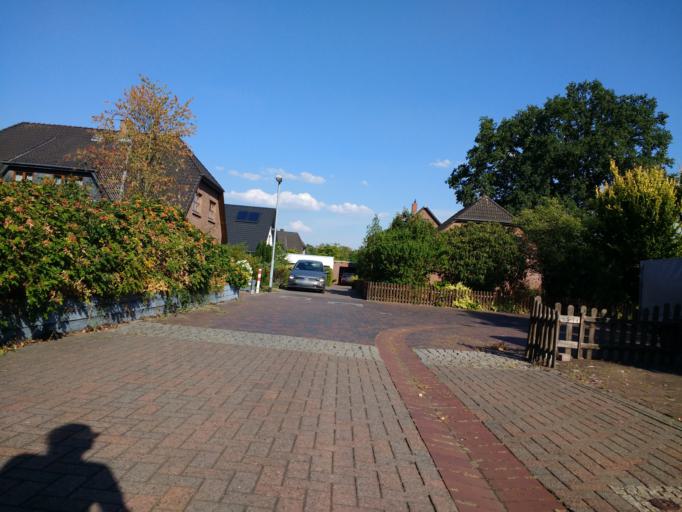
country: DE
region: Lower Saxony
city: Gifhorn
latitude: 52.4667
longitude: 10.5573
